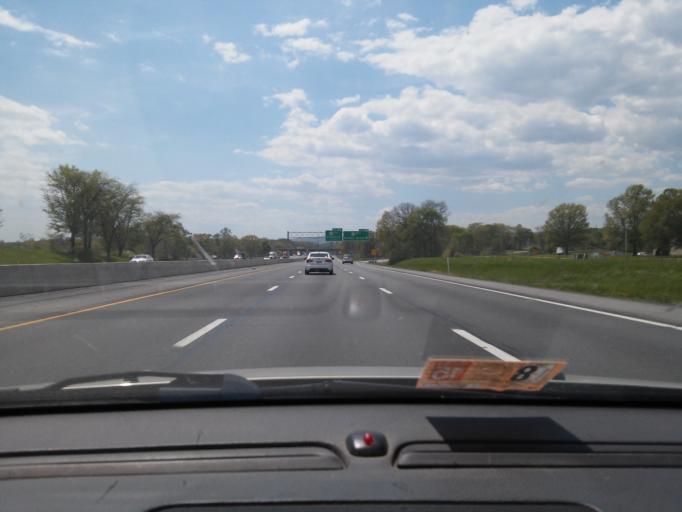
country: US
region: West Virginia
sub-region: Berkeley County
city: Martinsburg
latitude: 39.4992
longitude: -77.9530
